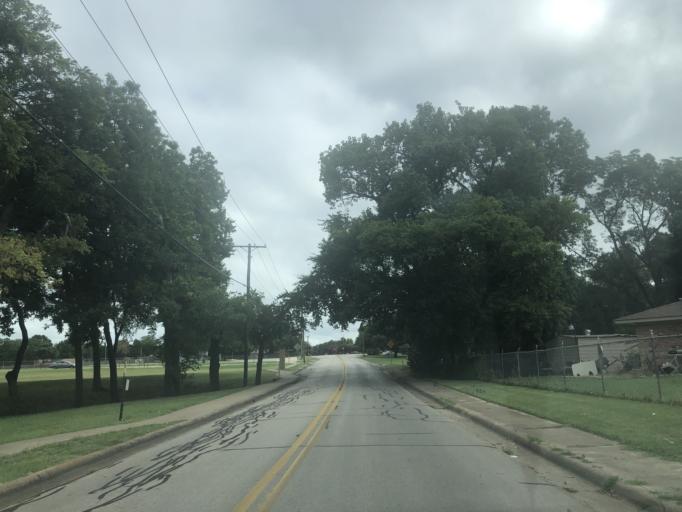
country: US
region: Texas
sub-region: Dallas County
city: Duncanville
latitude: 32.6554
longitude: -96.9174
